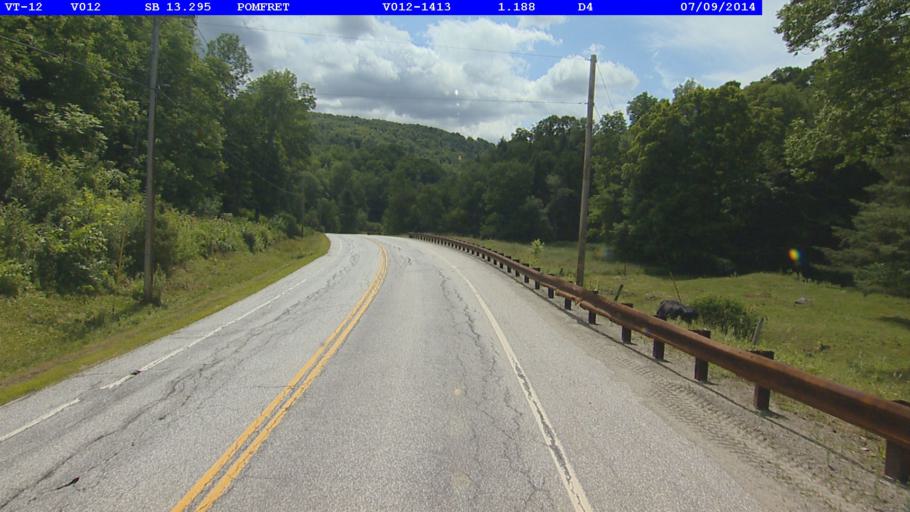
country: US
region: Vermont
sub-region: Windsor County
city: Woodstock
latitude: 43.6723
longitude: -72.5789
